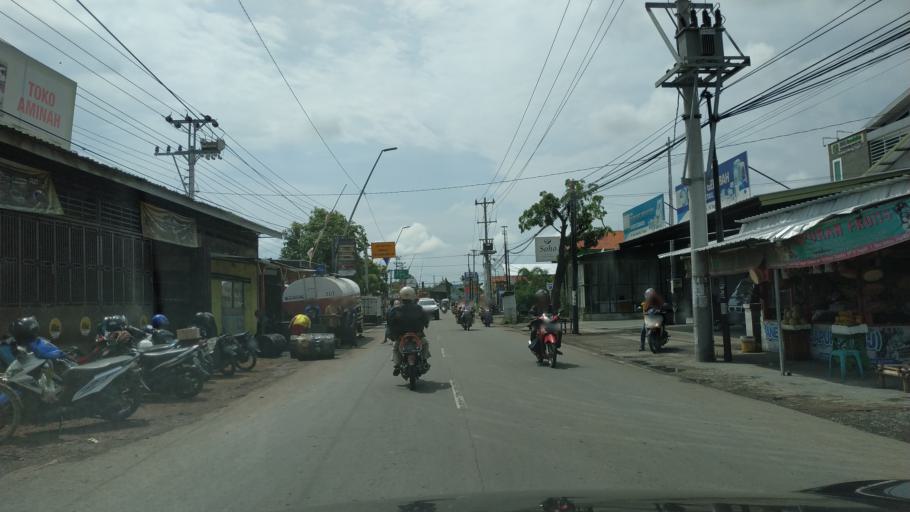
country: ID
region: Central Java
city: Tegal
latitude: -6.8849
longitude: 109.1268
